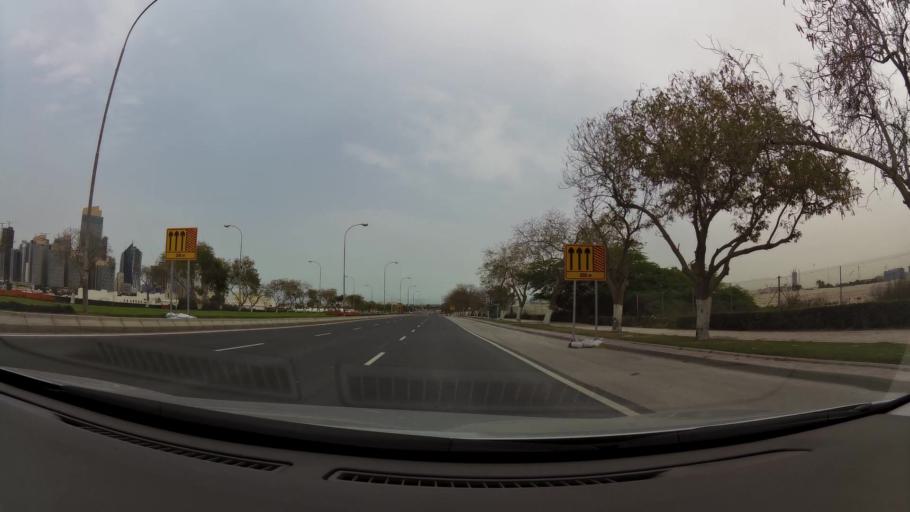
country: QA
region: Baladiyat ad Dawhah
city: Doha
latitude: 25.3126
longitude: 51.5081
